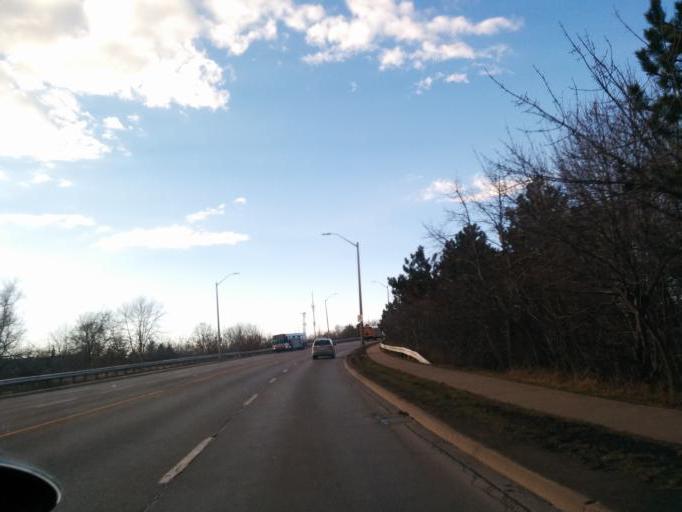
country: CA
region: Ontario
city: Mississauga
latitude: 43.5636
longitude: -79.6288
